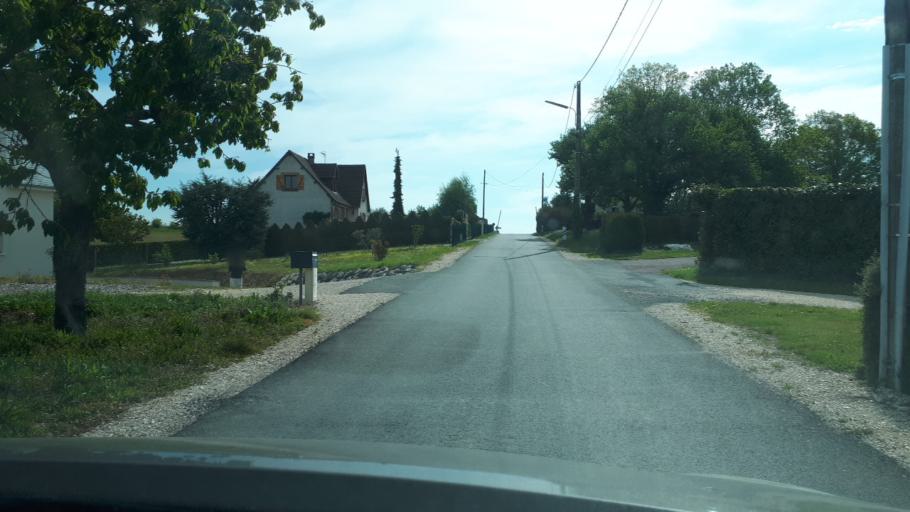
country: FR
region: Centre
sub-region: Departement du Loir-et-Cher
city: Naveil
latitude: 47.7714
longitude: 1.0156
